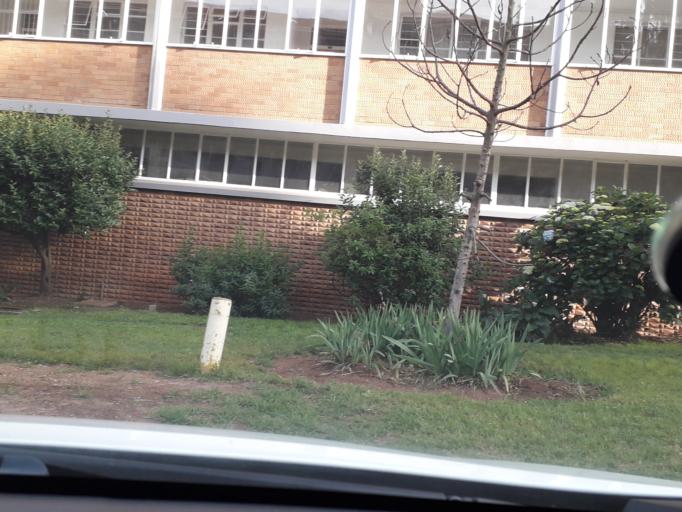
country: ZA
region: Gauteng
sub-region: City of Johannesburg Metropolitan Municipality
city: Johannesburg
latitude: -26.1351
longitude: 28.0868
